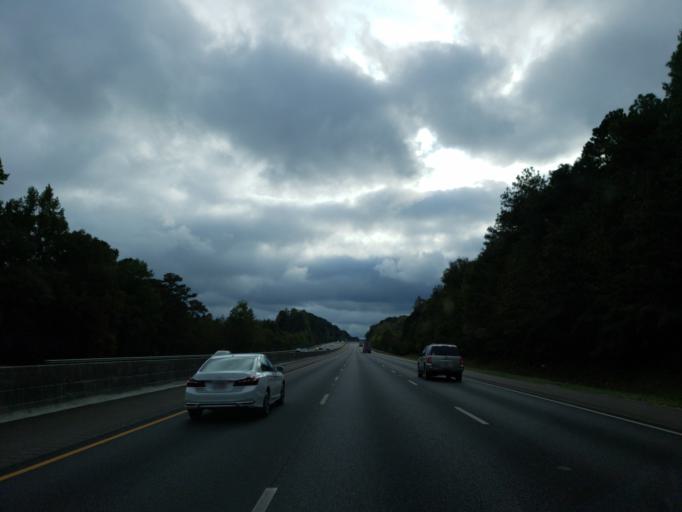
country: US
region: Alabama
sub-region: Bibb County
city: Woodstock
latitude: 33.2281
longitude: -87.1720
